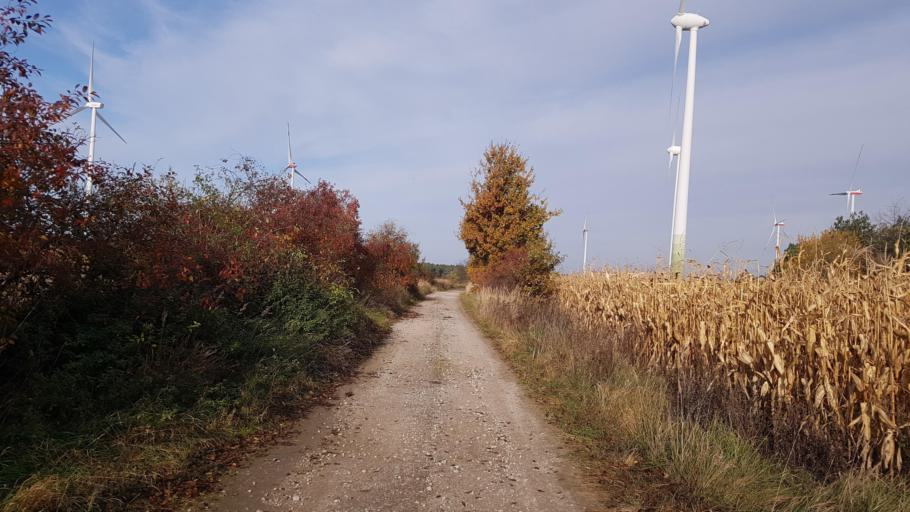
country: DE
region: Brandenburg
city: Treuenbrietzen
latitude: 52.0086
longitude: 12.8805
